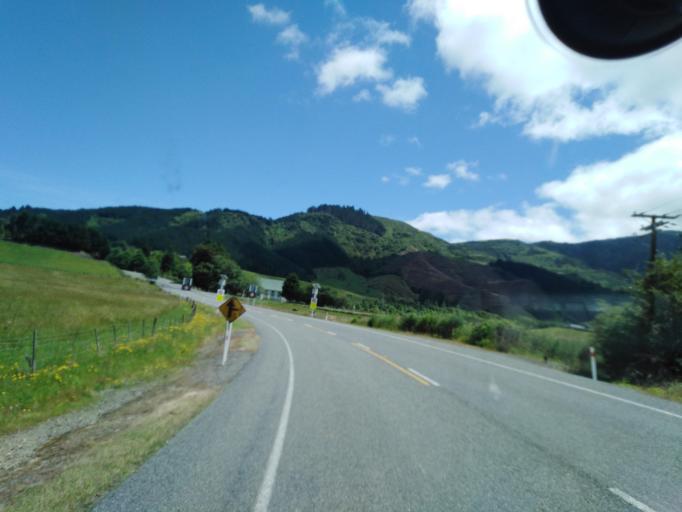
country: NZ
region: Nelson
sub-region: Nelson City
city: Nelson
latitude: -41.2121
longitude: 173.3957
